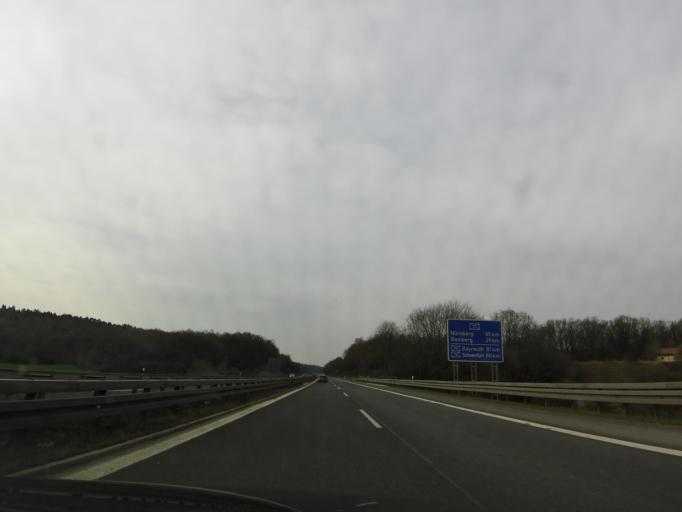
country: DE
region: Bavaria
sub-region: Upper Franconia
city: Bad Staffelstein
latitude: 50.0899
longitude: 11.0028
